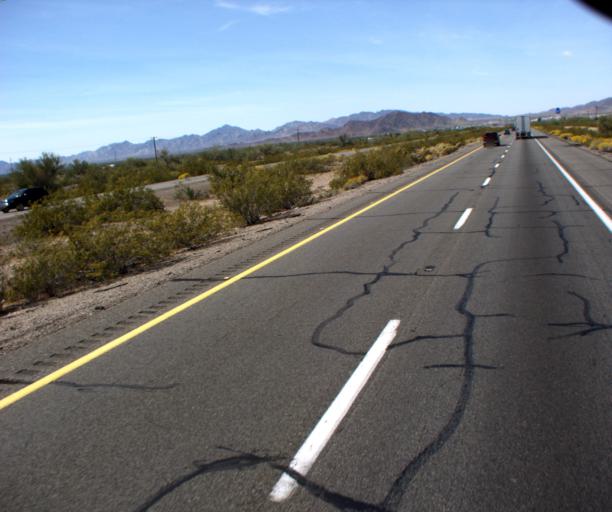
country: US
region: Arizona
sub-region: La Paz County
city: Quartzsite
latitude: 33.6682
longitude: -114.1776
